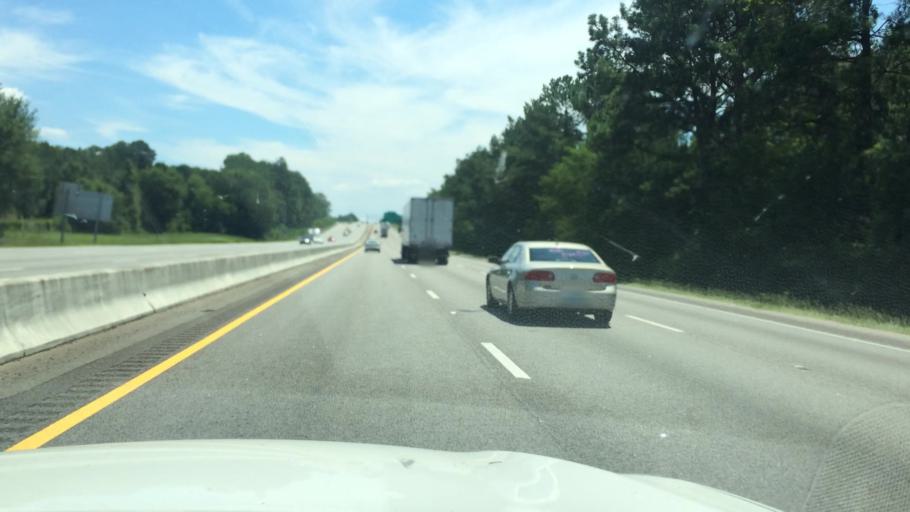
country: US
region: South Carolina
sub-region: Richland County
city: Dentsville
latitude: 34.0731
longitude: -80.9881
